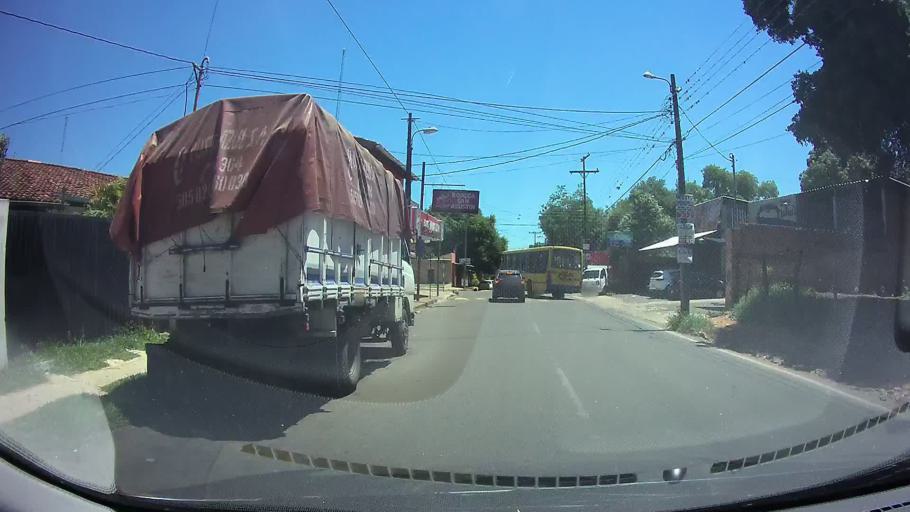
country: PY
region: Central
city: San Lorenzo
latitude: -25.2580
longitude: -57.4883
